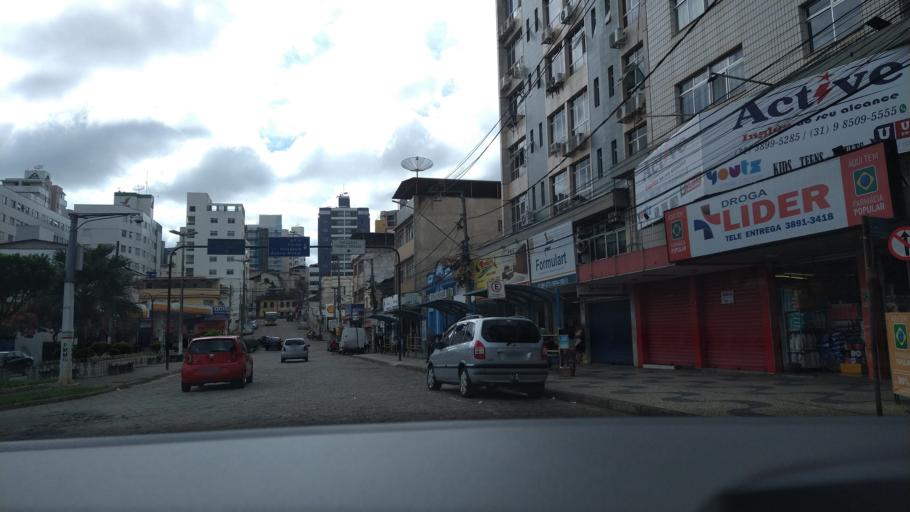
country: BR
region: Minas Gerais
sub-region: Vicosa
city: Vicosa
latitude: -20.7562
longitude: -42.8801
